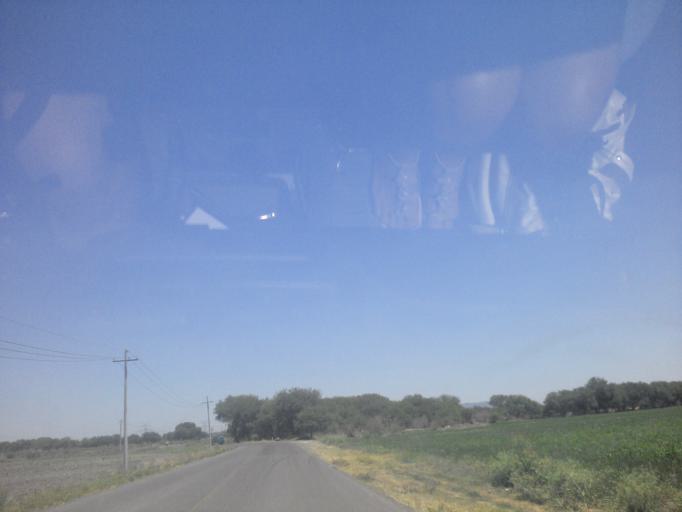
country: MX
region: Guanajuato
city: San Roque
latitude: 20.9530
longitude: -101.8864
